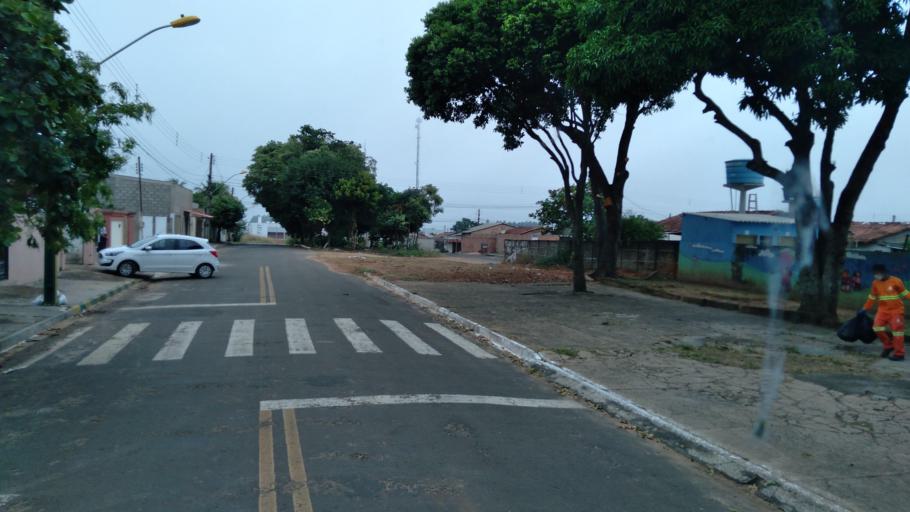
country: BR
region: Goias
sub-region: Mineiros
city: Mineiros
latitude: -17.5742
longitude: -52.5402
